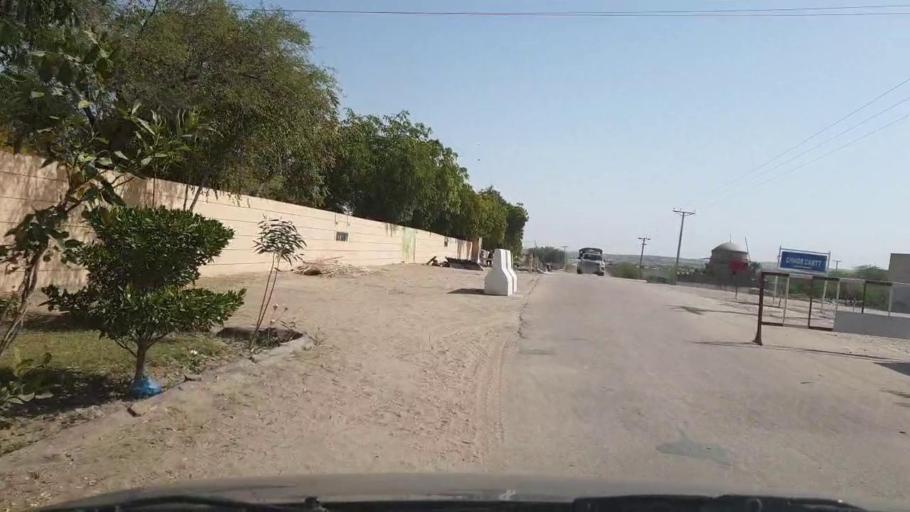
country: PK
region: Sindh
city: Chor
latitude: 25.5149
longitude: 69.8066
